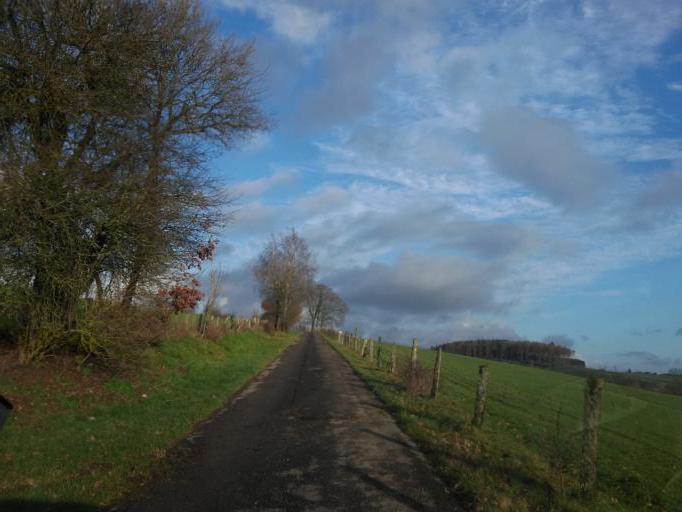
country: BE
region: Wallonia
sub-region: Province du Luxembourg
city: Neufchateau
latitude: 49.8060
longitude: 5.4372
